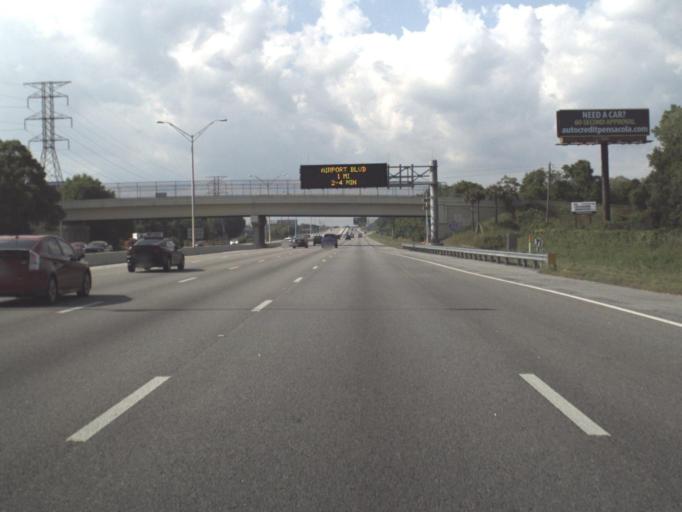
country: US
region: Florida
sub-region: Escambia County
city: Brent
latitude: 30.4604
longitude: -87.2250
